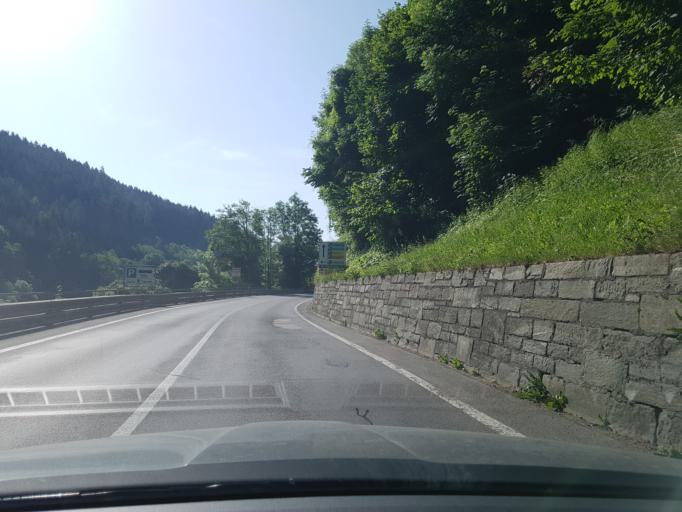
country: AT
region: Carinthia
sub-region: Politischer Bezirk Spittal an der Drau
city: Spittal an der Drau
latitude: 46.8022
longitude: 13.4966
